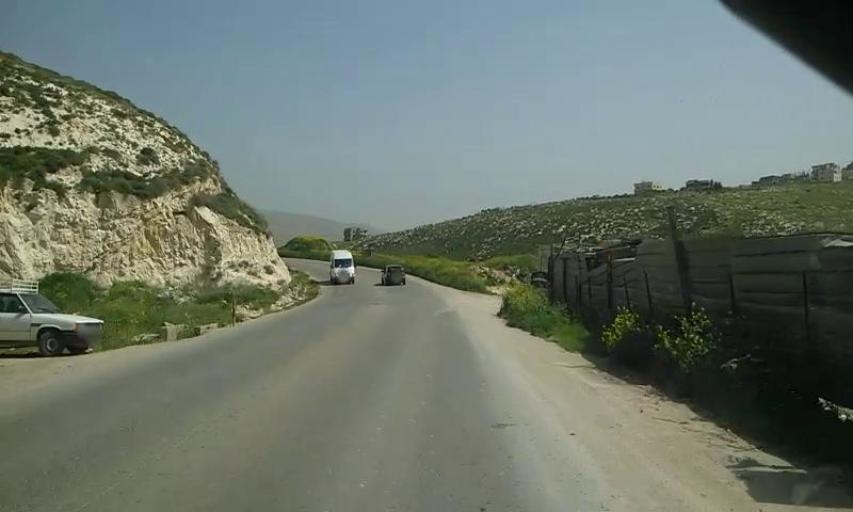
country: PS
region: West Bank
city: Tammun
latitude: 32.2923
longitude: 35.3511
